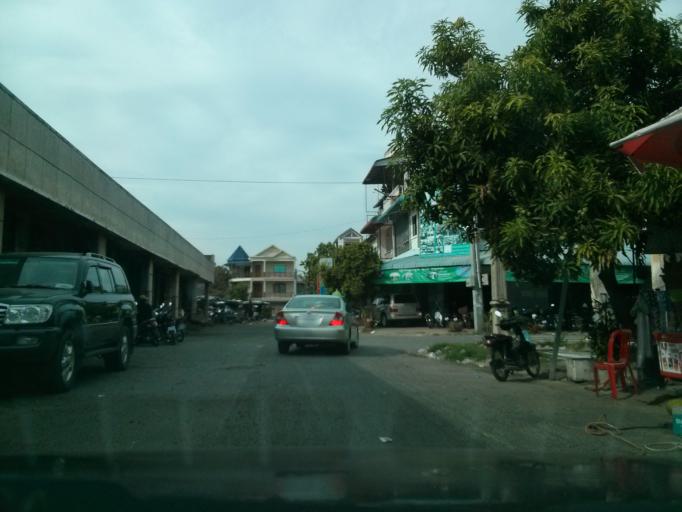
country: KH
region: Takeo
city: Takeo
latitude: 10.9934
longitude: 104.7855
